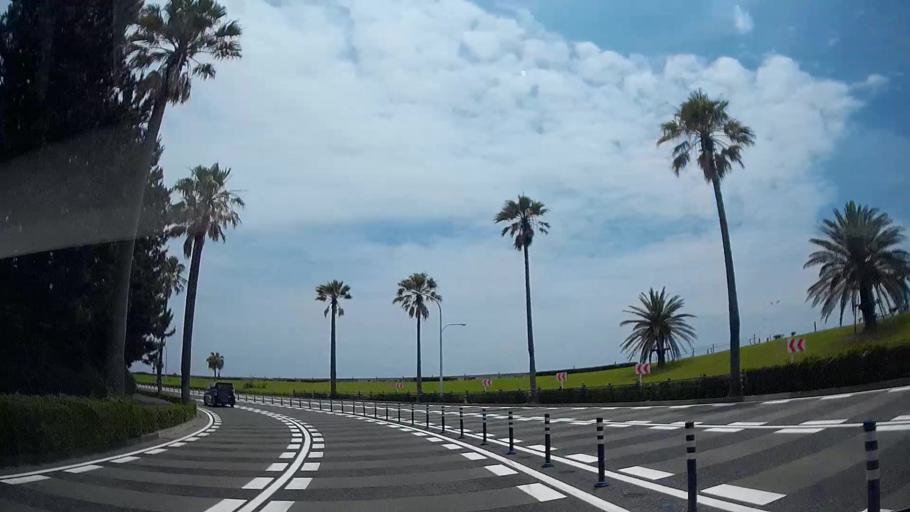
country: JP
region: Tokyo
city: Urayasu
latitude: 35.6262
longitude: 139.8729
